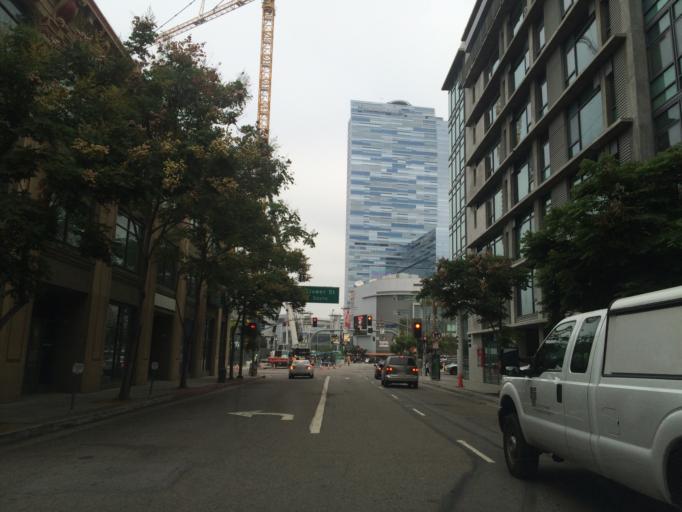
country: US
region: California
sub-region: Los Angeles County
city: Los Angeles
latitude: 34.0426
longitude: -118.2635
